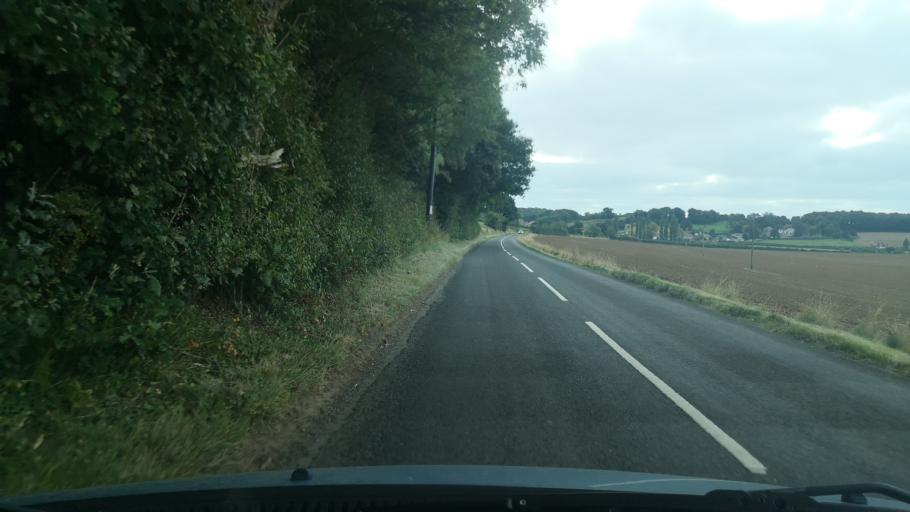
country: GB
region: England
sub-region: City and Borough of Wakefield
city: Darrington
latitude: 53.6552
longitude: -1.2737
